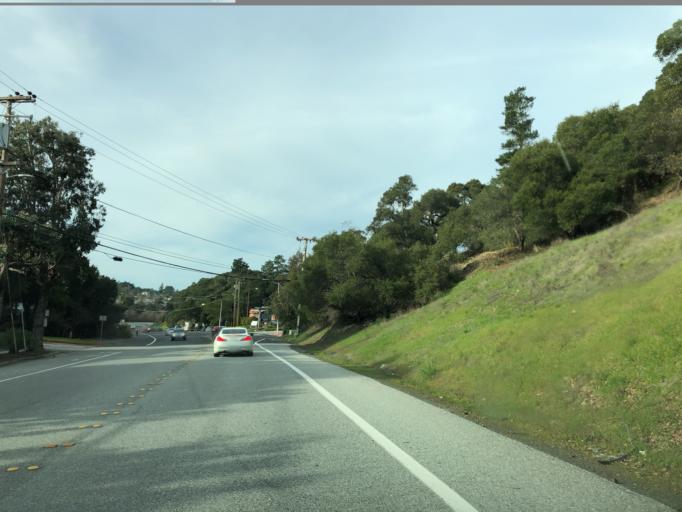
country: US
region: California
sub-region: San Mateo County
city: Highlands-Baywood Park
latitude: 37.5189
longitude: -122.3368
